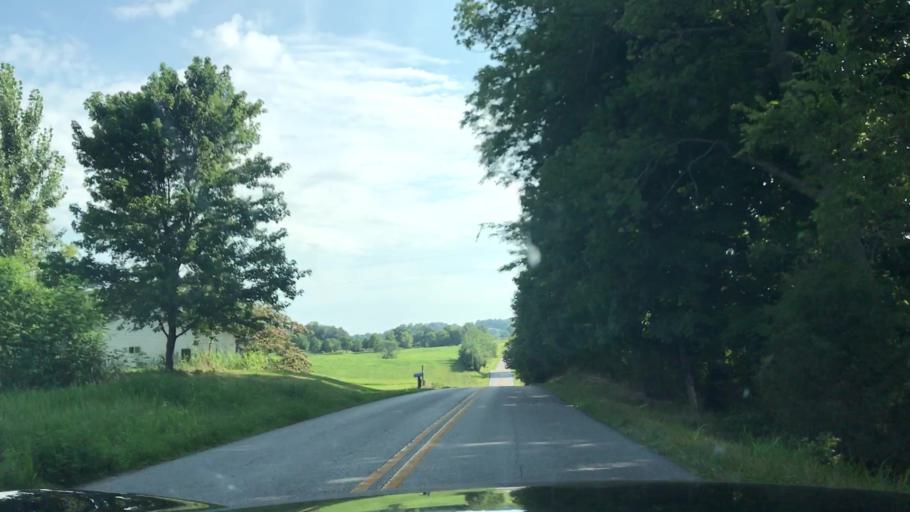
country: US
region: Kentucky
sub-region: Hart County
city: Munfordville
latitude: 37.2237
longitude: -85.7218
